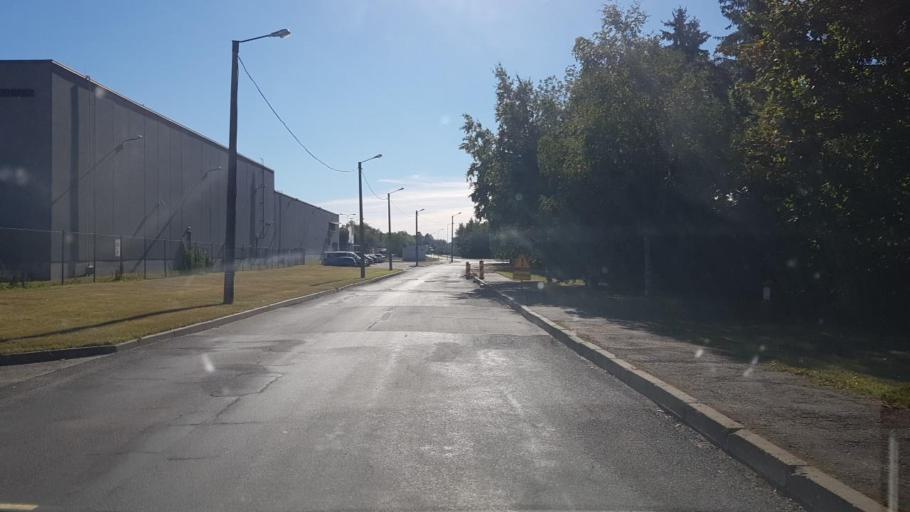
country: EE
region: Harju
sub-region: Tallinna linn
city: Tallinn
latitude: 59.4077
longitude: 24.8145
